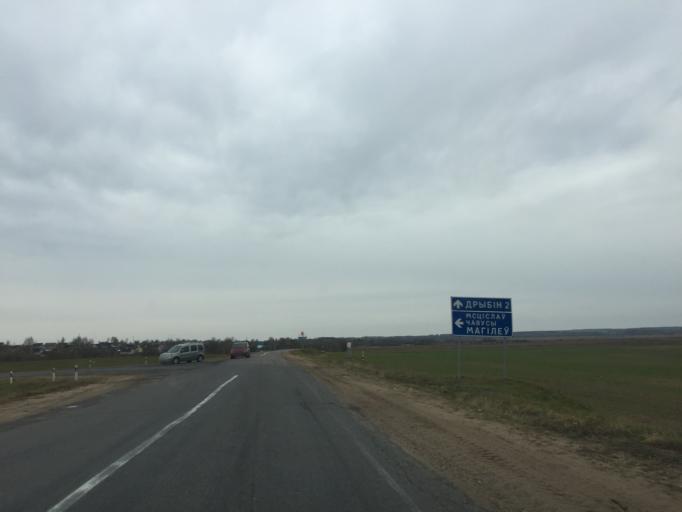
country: BY
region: Mogilev
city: Drybin
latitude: 54.1386
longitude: 31.1101
